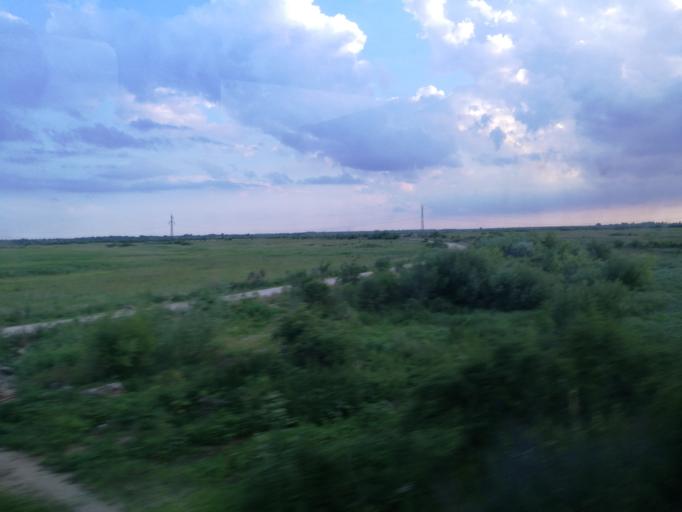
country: RO
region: Dambovita
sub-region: Comuna Produlesti
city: Costestii din Deal
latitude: 44.6758
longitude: 25.4930
